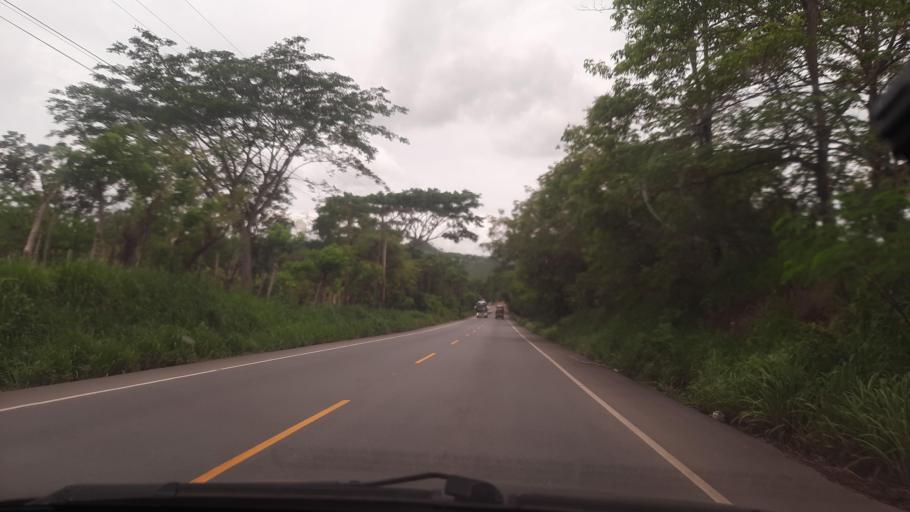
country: GT
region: Zacapa
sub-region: Municipio de Zacapa
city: Gualan
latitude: 15.1684
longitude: -89.3077
